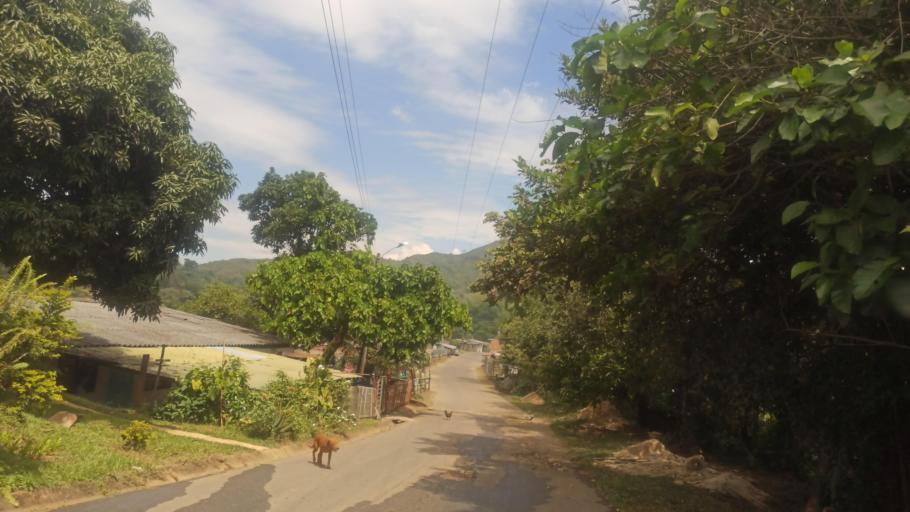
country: CO
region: Valle del Cauca
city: Jamundi
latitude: 3.1883
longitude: -76.6311
